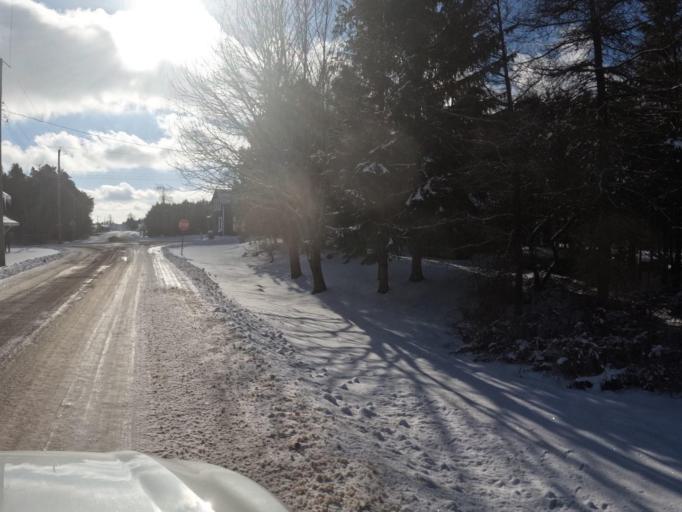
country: CA
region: Ontario
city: Shelburne
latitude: 43.9824
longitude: -80.4056
